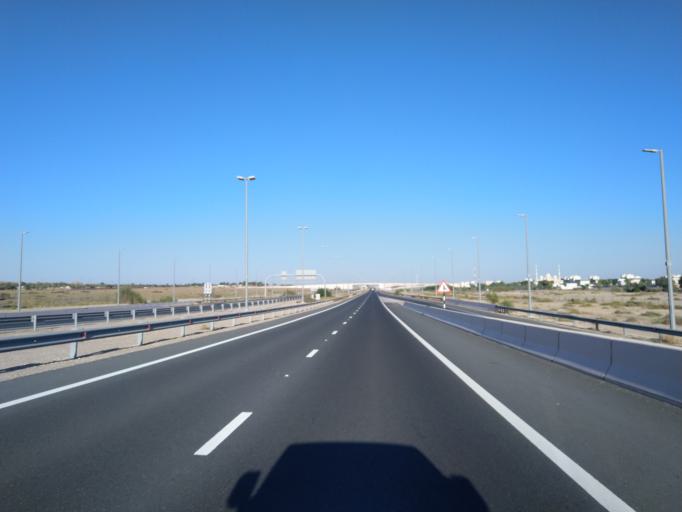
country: OM
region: Al Buraimi
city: Al Buraymi
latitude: 24.5136
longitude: 55.4890
